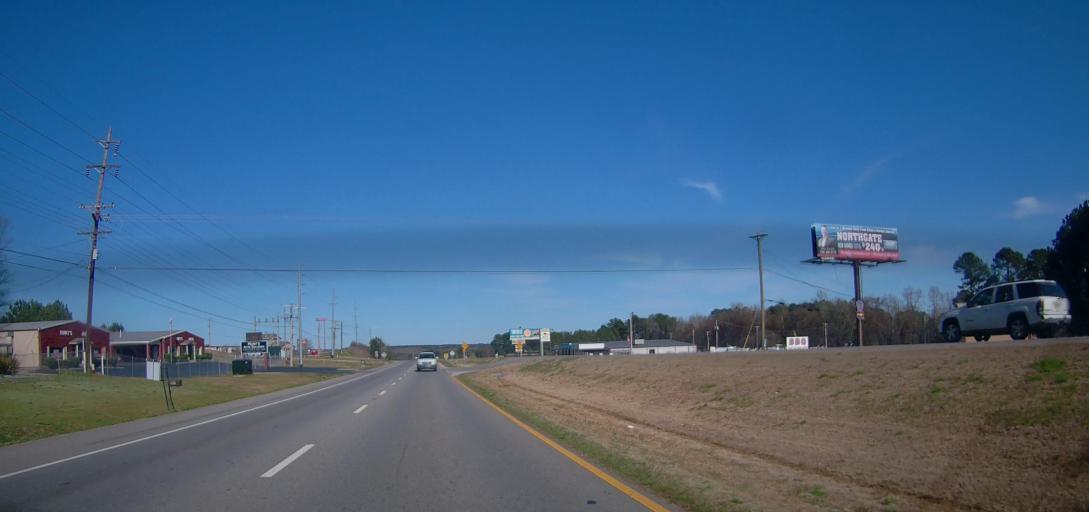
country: US
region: Alabama
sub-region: Lauderdale County
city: Killen
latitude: 34.8444
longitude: -87.5851
